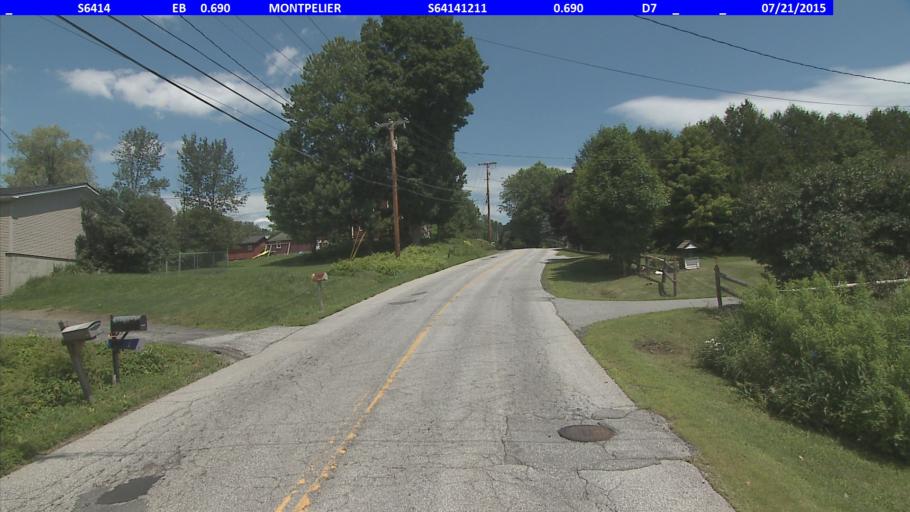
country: US
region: Vermont
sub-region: Washington County
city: Montpelier
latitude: 44.2439
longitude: -72.5317
